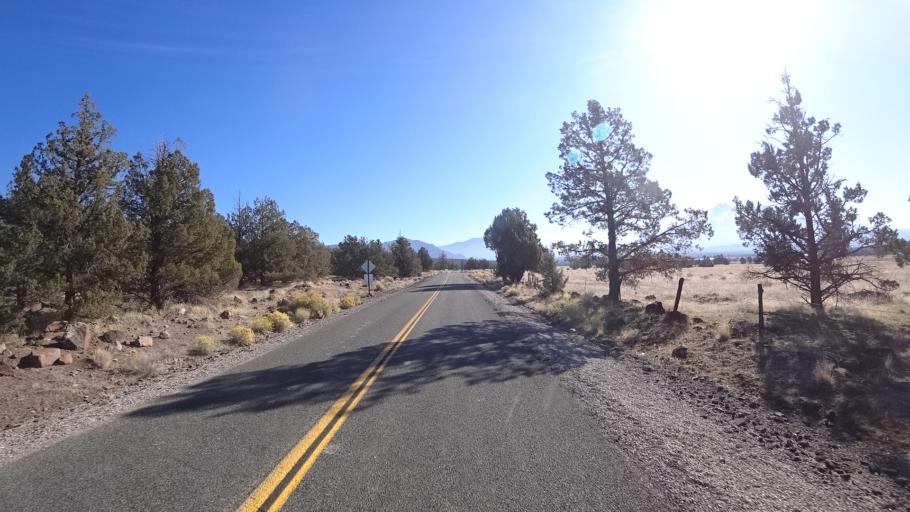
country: US
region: California
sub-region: Siskiyou County
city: Weed
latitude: 41.6023
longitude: -122.3041
